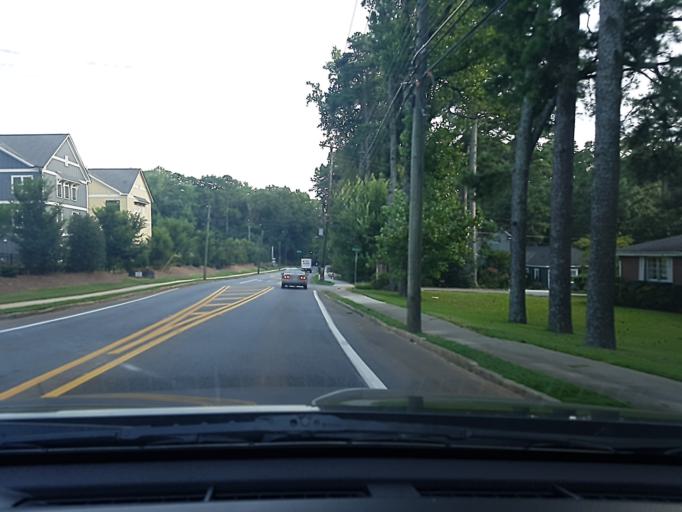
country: US
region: Georgia
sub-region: DeKalb County
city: North Atlanta
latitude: 33.8410
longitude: -84.3443
